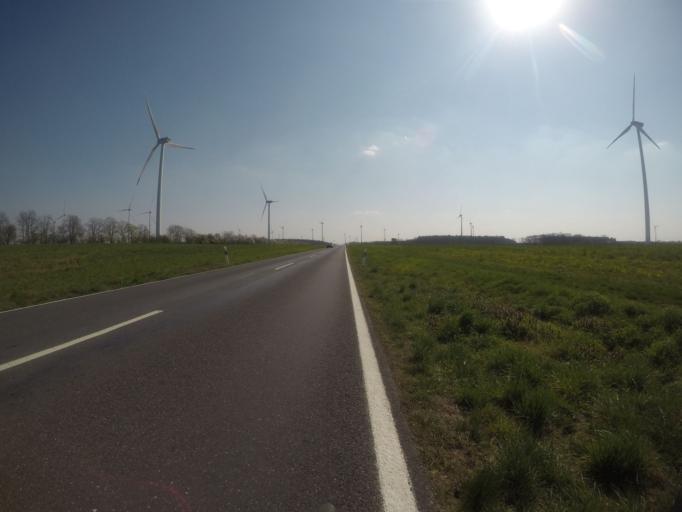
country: DE
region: Brandenburg
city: Nauen
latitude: 52.5475
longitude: 12.8732
